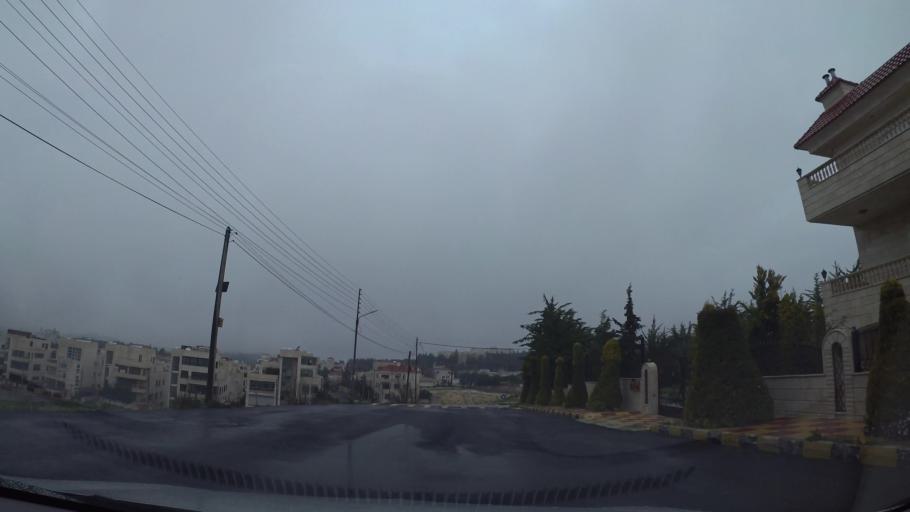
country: JO
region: Amman
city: Al Jubayhah
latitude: 32.0085
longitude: 35.8259
